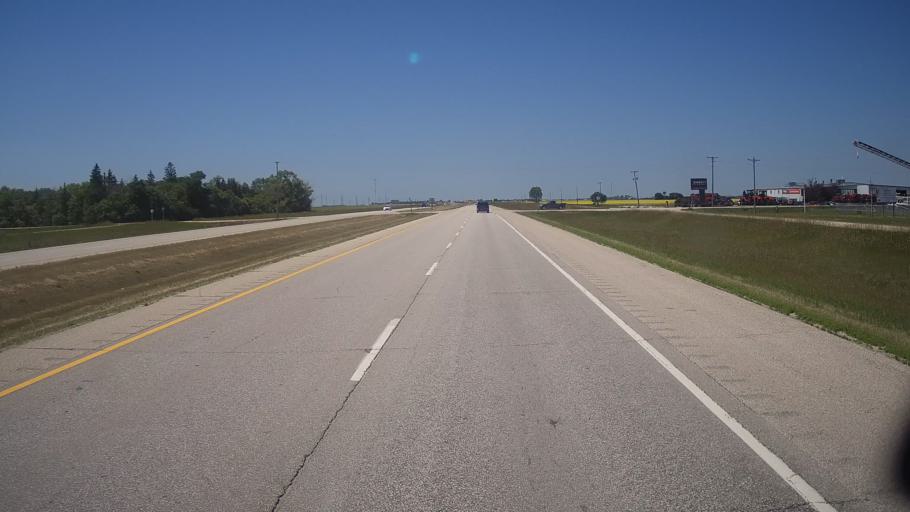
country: CA
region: Manitoba
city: Stonewall
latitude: 49.9900
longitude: -97.2734
